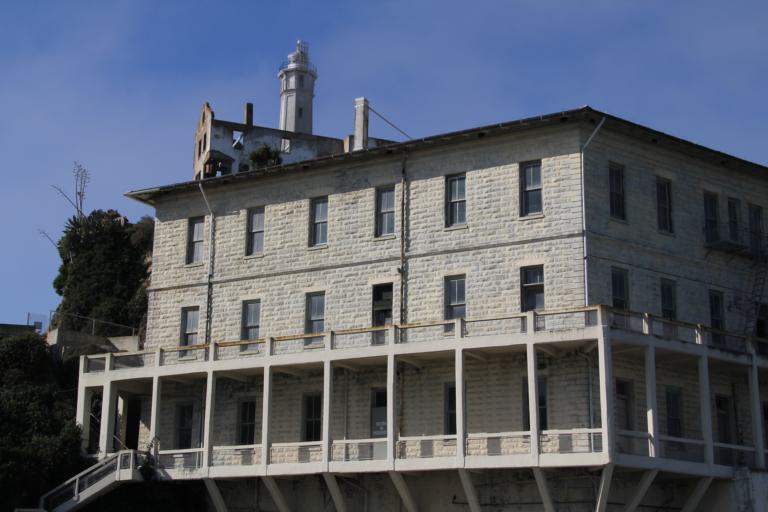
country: US
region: California
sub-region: San Francisco County
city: San Francisco
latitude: 37.8264
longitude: -122.4206
